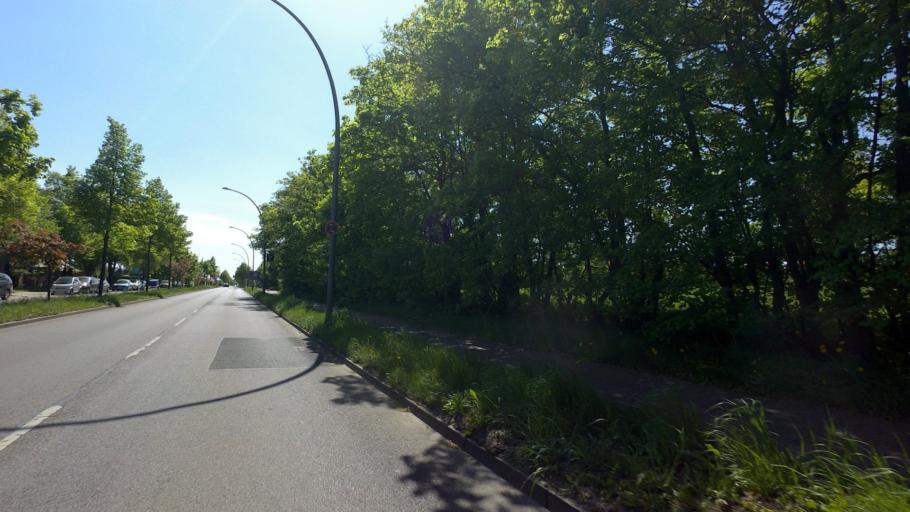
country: DE
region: Brandenburg
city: Schonefeld
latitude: 52.4025
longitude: 13.5125
